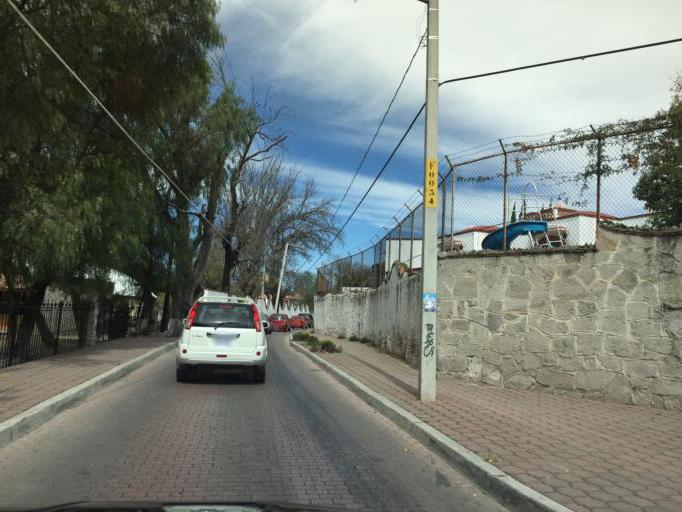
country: MX
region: Queretaro
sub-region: Tequisquiapan
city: Tequisquiapan
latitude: 20.5235
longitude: -99.8890
